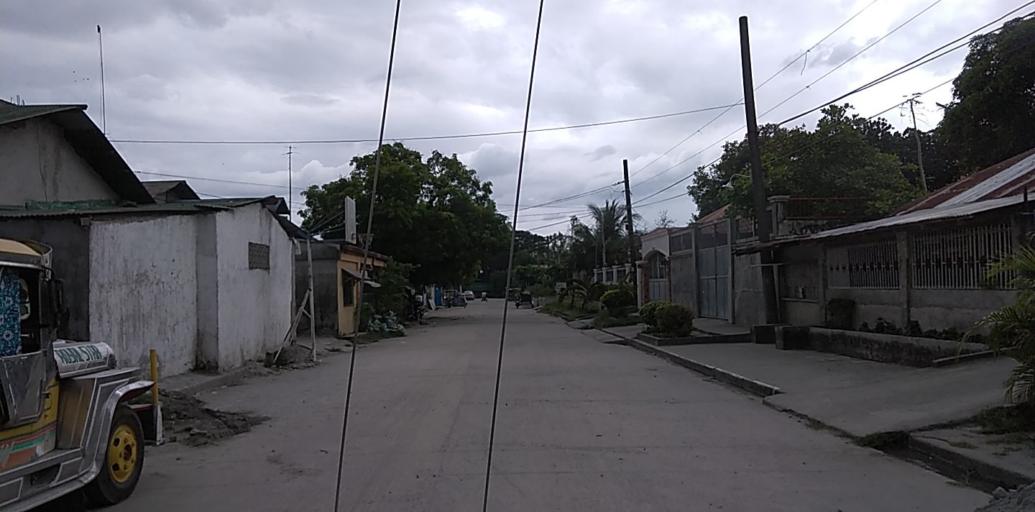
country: PH
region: Central Luzon
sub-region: Province of Pampanga
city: Pio
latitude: 15.0416
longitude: 120.5284
